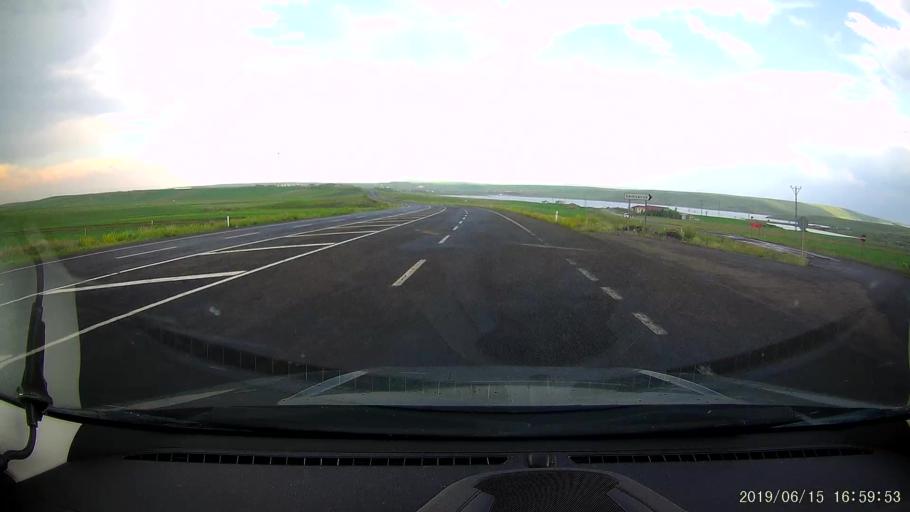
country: TR
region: Kars
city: Susuz
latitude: 40.7459
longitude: 43.1544
